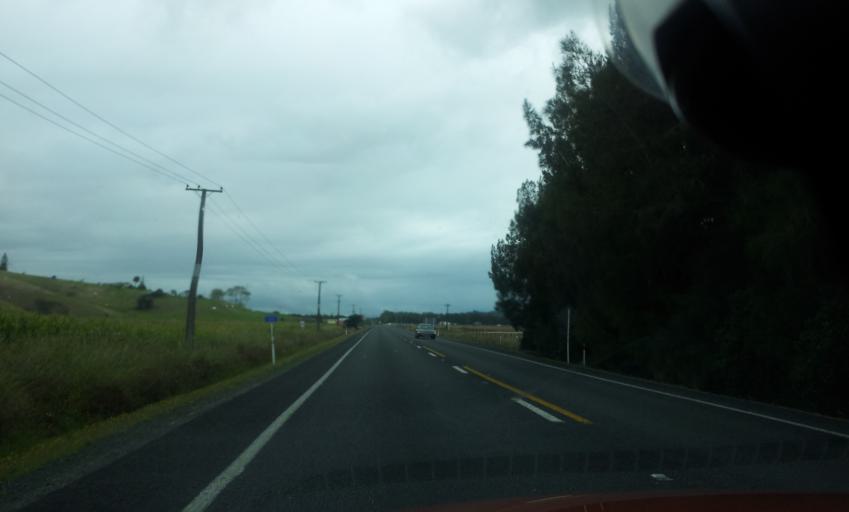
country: NZ
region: Northland
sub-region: Whangarei
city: Ruakaka
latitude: -35.8965
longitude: 174.4395
